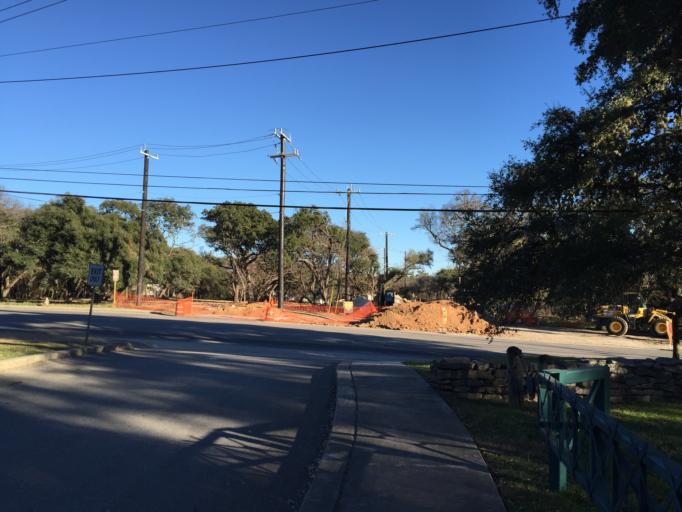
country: US
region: Texas
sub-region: Bexar County
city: Castle Hills
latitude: 29.5559
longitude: -98.4997
